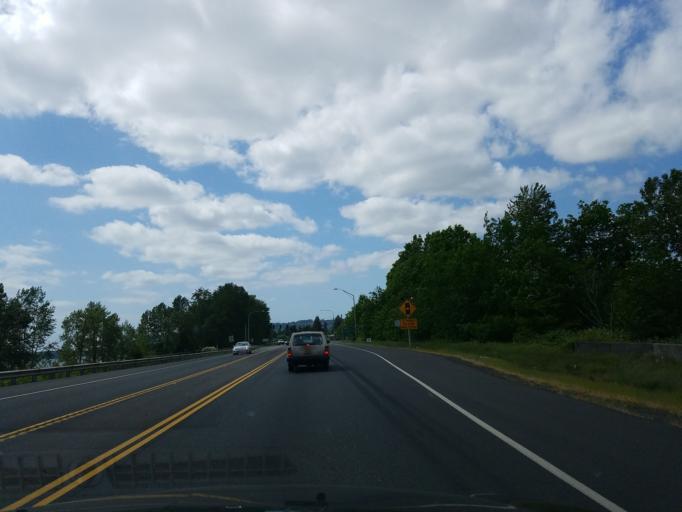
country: US
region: Washington
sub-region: Clark County
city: Washougal
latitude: 45.5760
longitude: -122.3537
